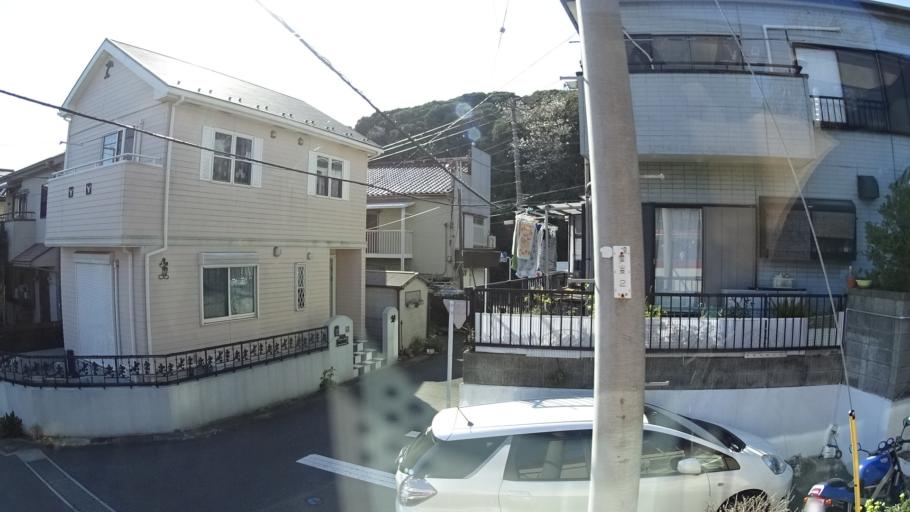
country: JP
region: Kanagawa
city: Miura
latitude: 35.1612
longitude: 139.6413
